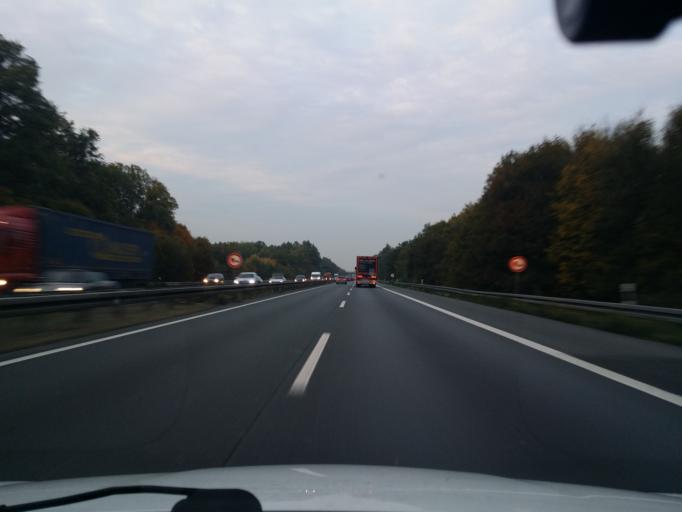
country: DE
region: Hesse
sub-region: Regierungsbezirk Darmstadt
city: Alsbach-Hahnlein
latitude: 49.7448
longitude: 8.5435
